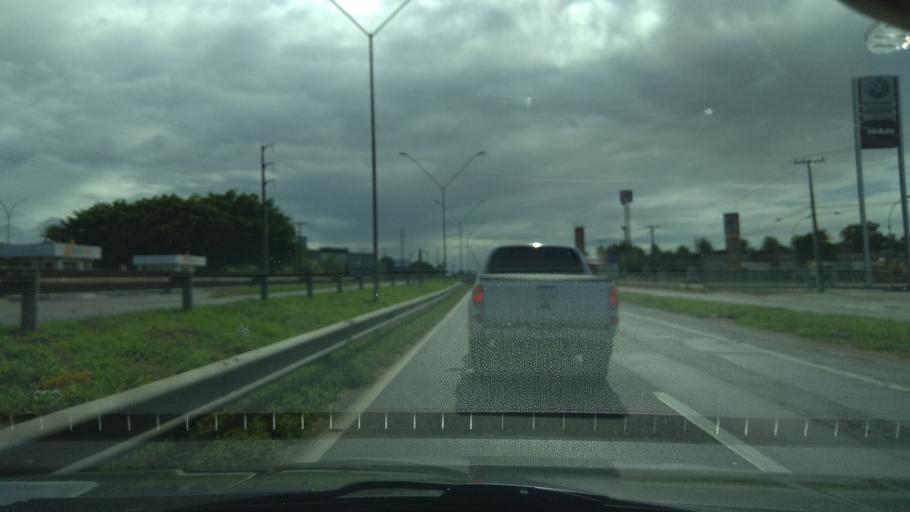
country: BR
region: Bahia
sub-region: Feira De Santana
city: Feira de Santana
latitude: -12.3056
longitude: -38.8908
